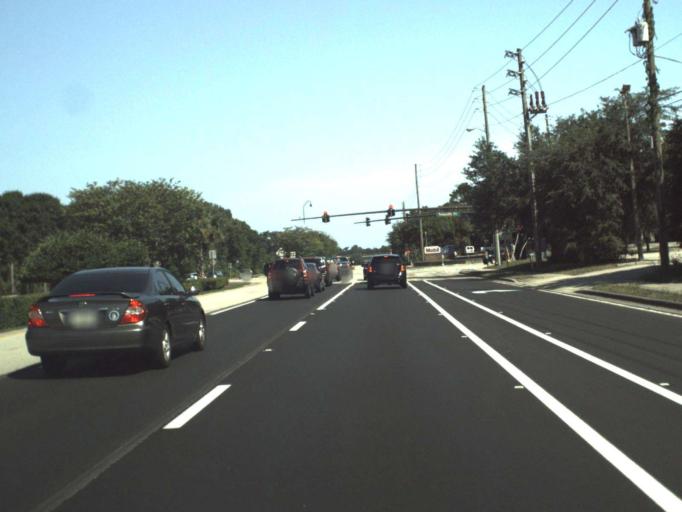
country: US
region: Florida
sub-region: Seminole County
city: Winter Springs
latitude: 28.6974
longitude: -81.2632
